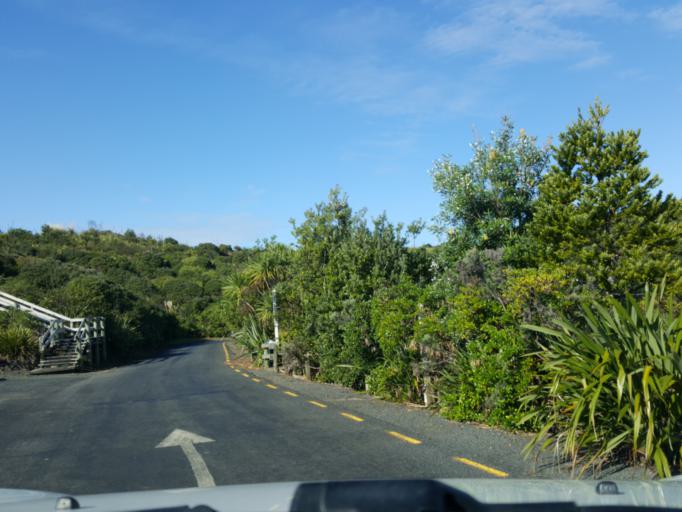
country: NZ
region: Waikato
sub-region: Waikato District
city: Raglan
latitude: -37.8183
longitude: 174.8302
